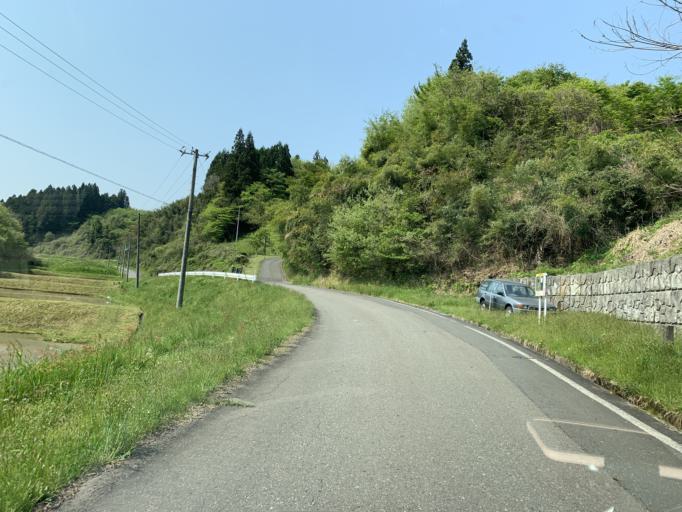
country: JP
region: Iwate
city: Ichinoseki
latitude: 38.8943
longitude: 141.1027
